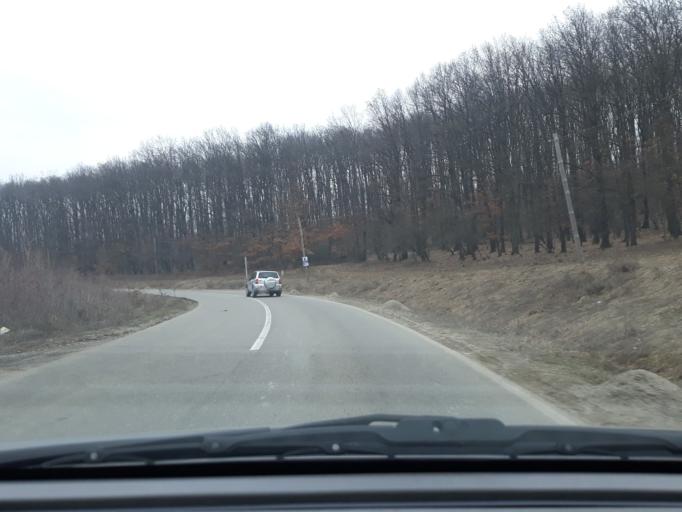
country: RO
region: Salaj
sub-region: Comuna Criseni
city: Criseni
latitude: 47.2371
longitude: 23.0733
